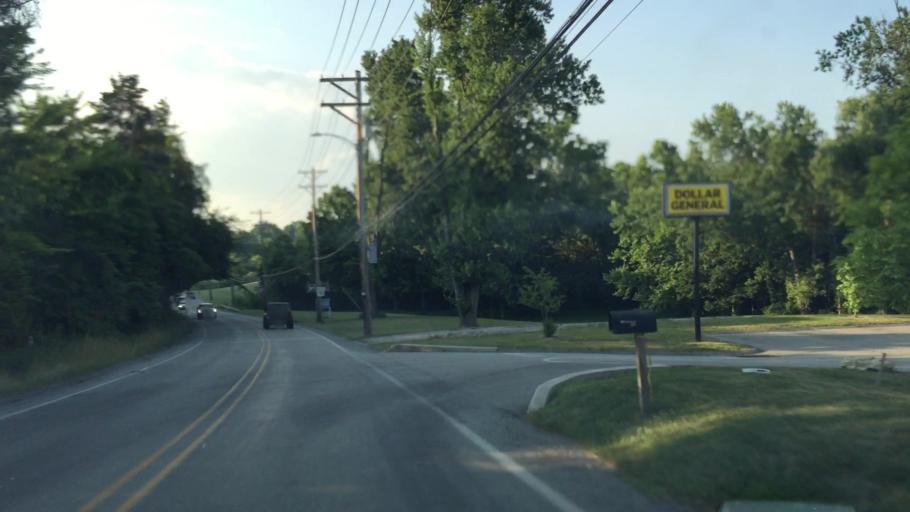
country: US
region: Pennsylvania
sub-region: Allegheny County
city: South Park Township
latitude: 40.2982
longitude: -79.9944
